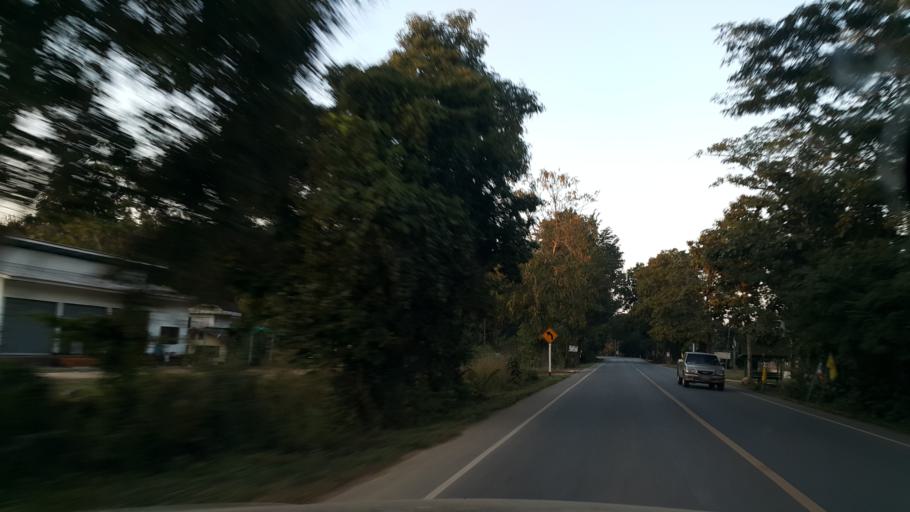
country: TH
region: Phrae
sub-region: Amphoe Wang Chin
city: Wang Chin
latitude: 17.8651
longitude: 99.6223
